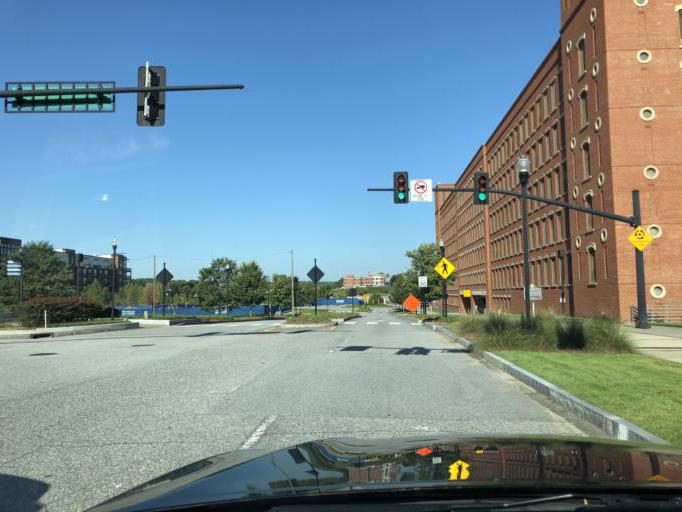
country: US
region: Alabama
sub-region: Russell County
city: Phenix City
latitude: 32.4725
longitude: -84.9931
